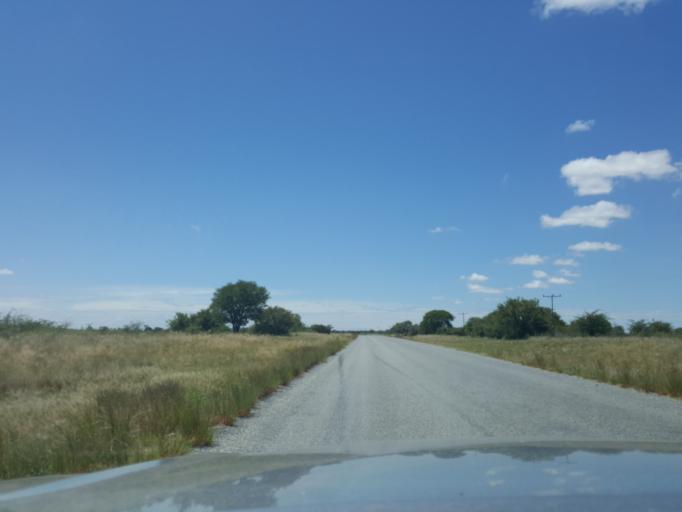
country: BW
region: Central
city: Nata
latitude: -20.1569
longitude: 25.8346
